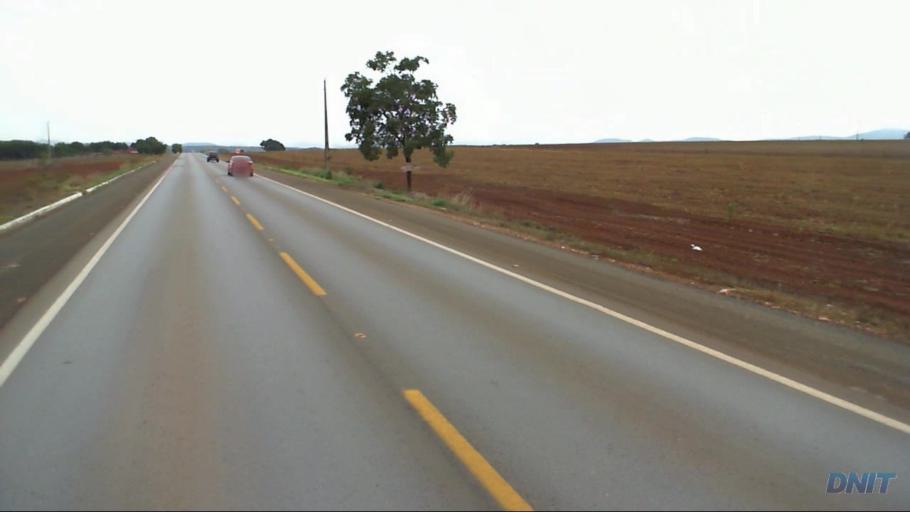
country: BR
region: Goias
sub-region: Uruacu
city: Uruacu
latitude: -14.6421
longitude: -49.1708
